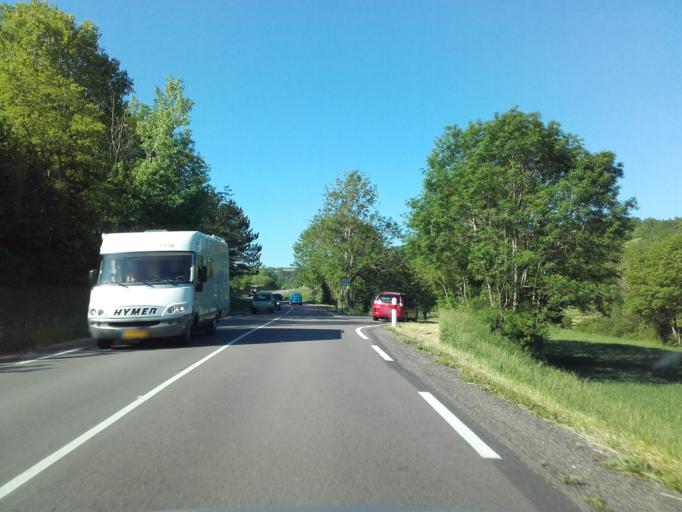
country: FR
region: Bourgogne
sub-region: Departement de la Cote-d'Or
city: Nolay
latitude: 46.9715
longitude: 4.6987
